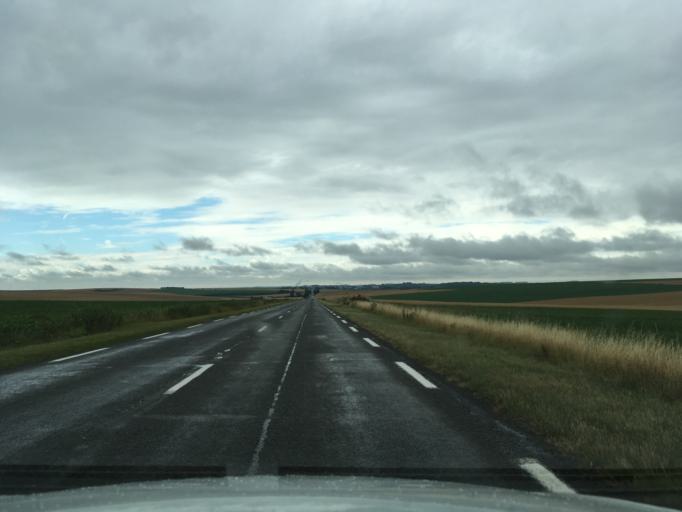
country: FR
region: Picardie
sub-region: Departement de l'Aisne
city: Origny-Sainte-Benoite
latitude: 49.8619
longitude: 3.5469
